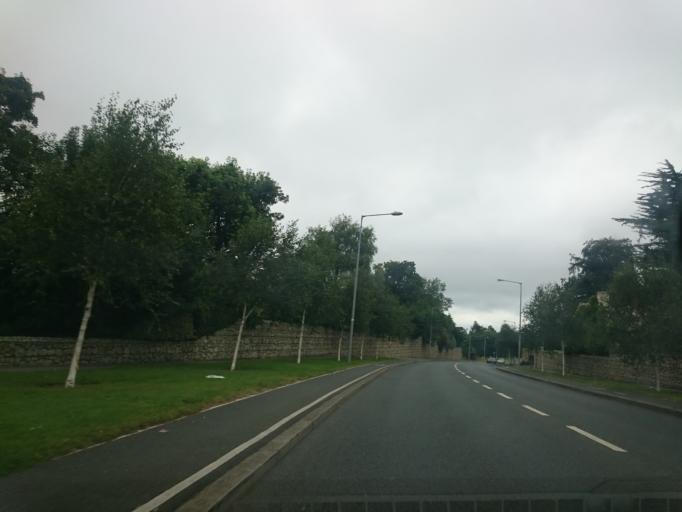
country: IE
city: Booterstown
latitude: 53.2808
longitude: -6.1967
